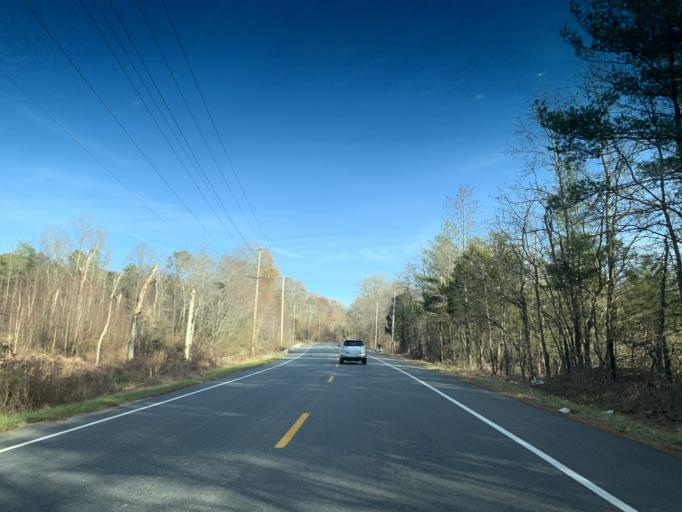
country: US
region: Maryland
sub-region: Cecil County
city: North East
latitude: 39.6044
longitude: -75.8883
